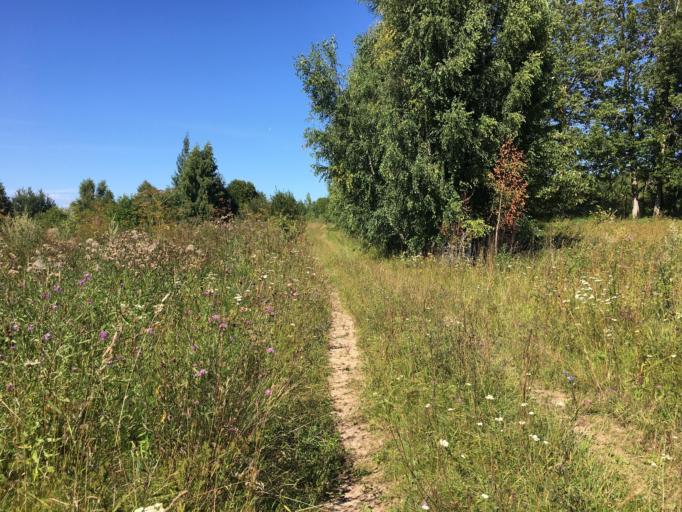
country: RU
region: Pskov
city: Izborsk
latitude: 57.8143
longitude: 27.9717
